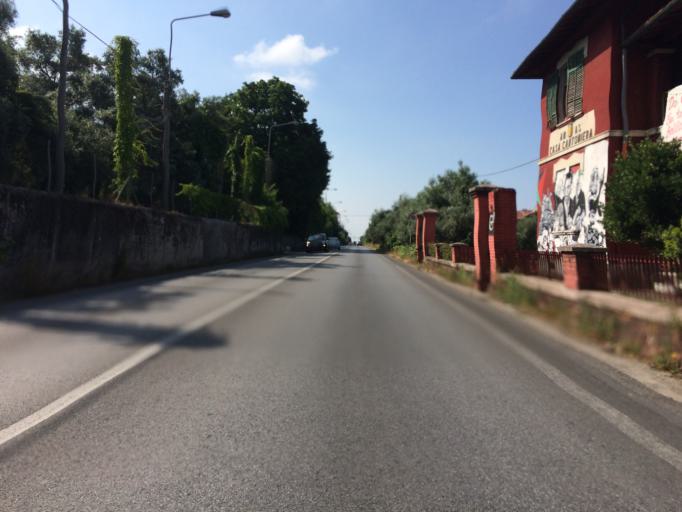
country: IT
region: Tuscany
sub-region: Provincia di Massa-Carrara
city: Capanne-Prato-Cinquale
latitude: 44.0127
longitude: 10.1579
